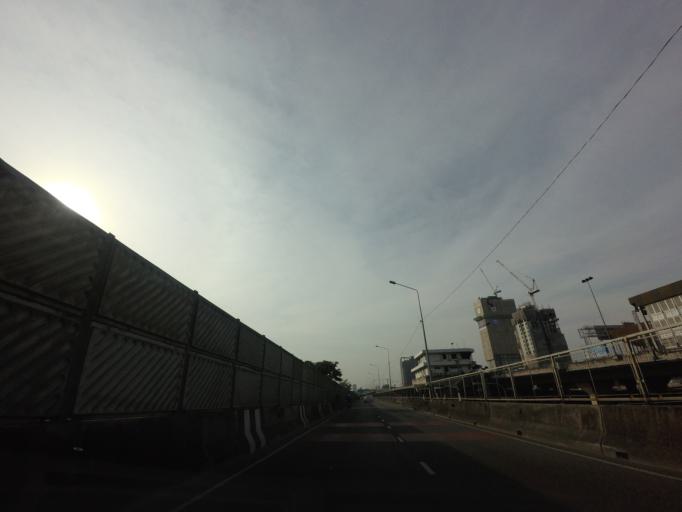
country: TH
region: Bangkok
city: Din Daeng
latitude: 13.7518
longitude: 100.5667
